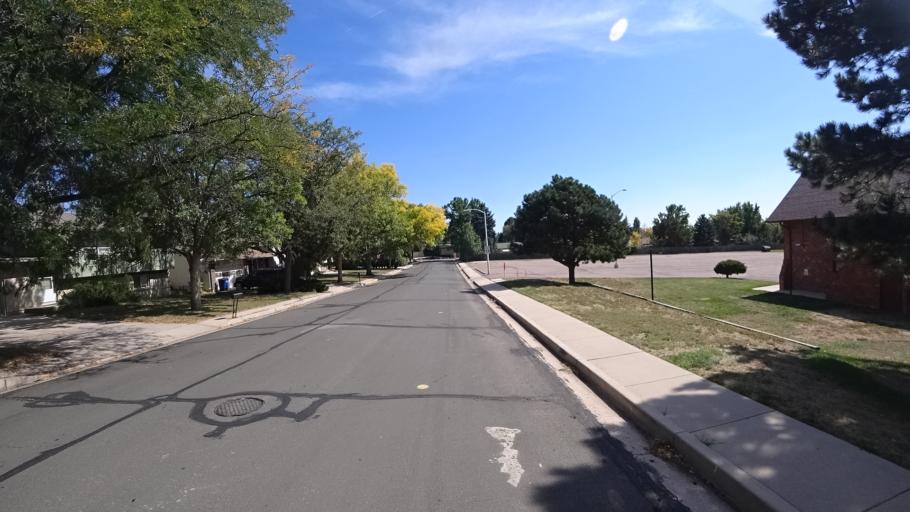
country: US
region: Colorado
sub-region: El Paso County
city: Cimarron Hills
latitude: 38.9062
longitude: -104.7634
